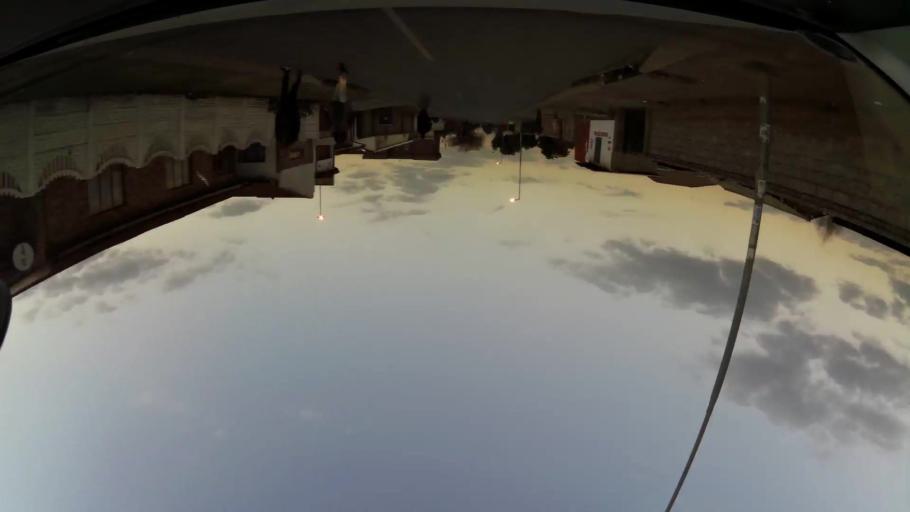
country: ZA
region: Gauteng
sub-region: City of Johannesburg Metropolitan Municipality
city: Soweto
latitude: -26.2703
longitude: 27.9067
